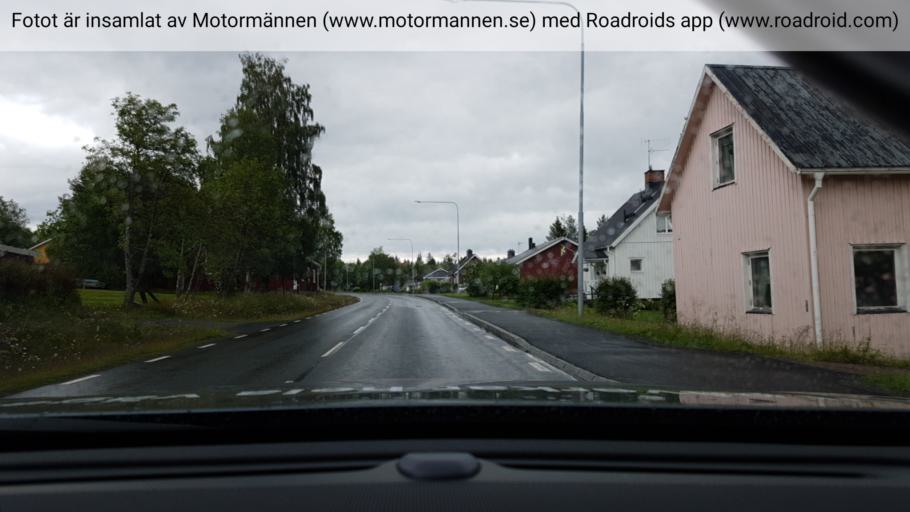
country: SE
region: Vaesterbotten
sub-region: Norsjo Kommun
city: Norsjoe
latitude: 65.2610
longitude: 19.6441
